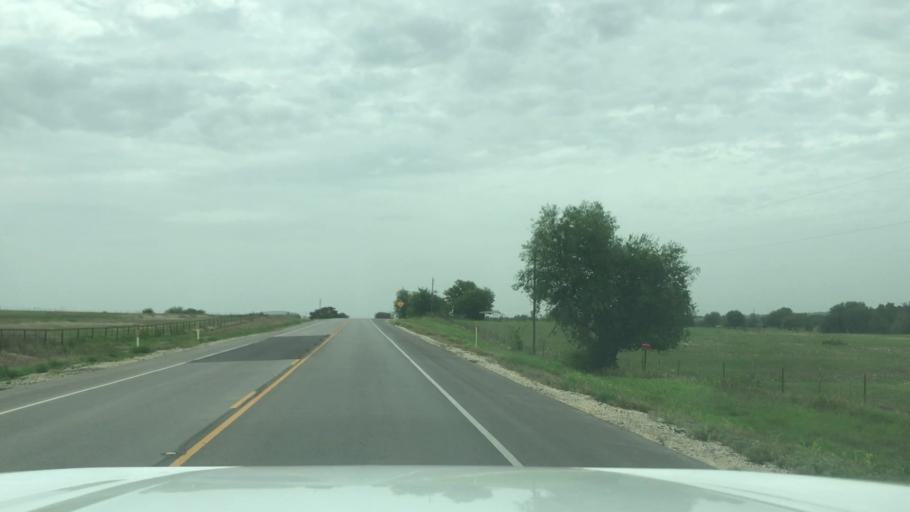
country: US
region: Texas
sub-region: Erath County
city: Dublin
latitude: 32.0658
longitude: -98.2165
